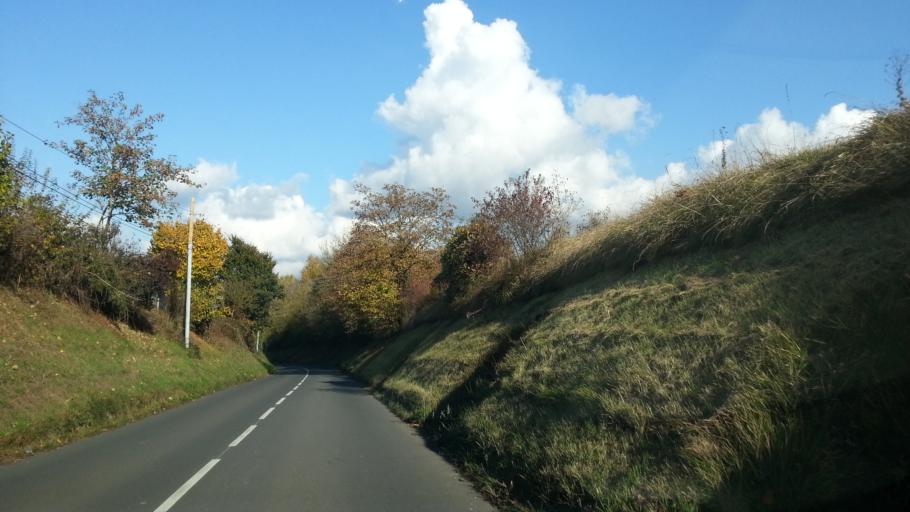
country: FR
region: Picardie
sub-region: Departement de l'Oise
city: Thiverny
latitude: 49.2496
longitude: 2.4039
